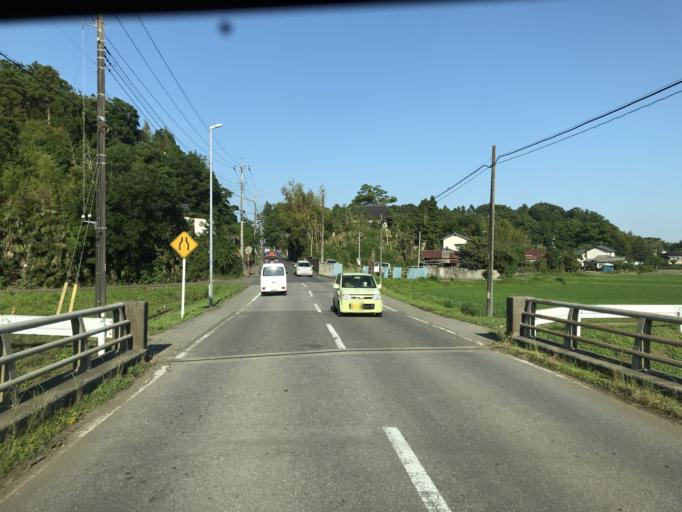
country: JP
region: Chiba
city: Yotsukaido
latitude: 35.6036
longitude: 140.2353
